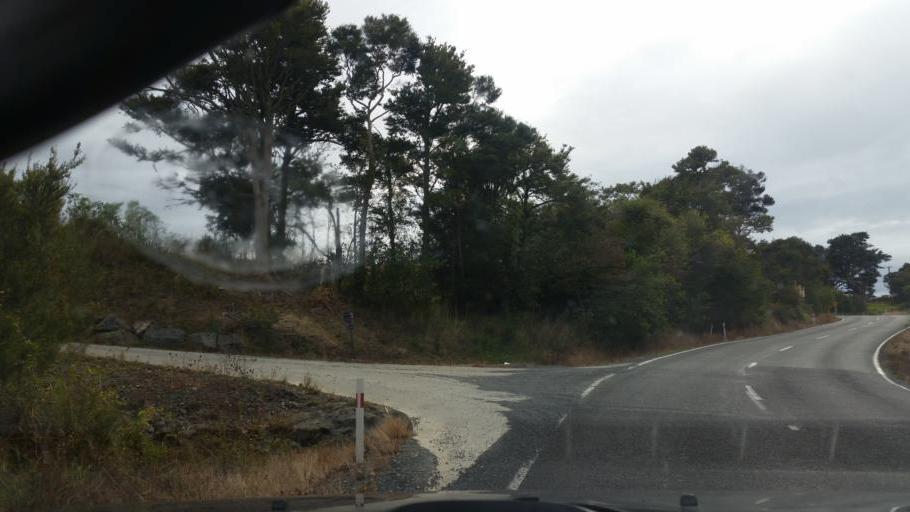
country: NZ
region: Auckland
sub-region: Auckland
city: Wellsford
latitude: -36.1531
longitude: 174.4679
